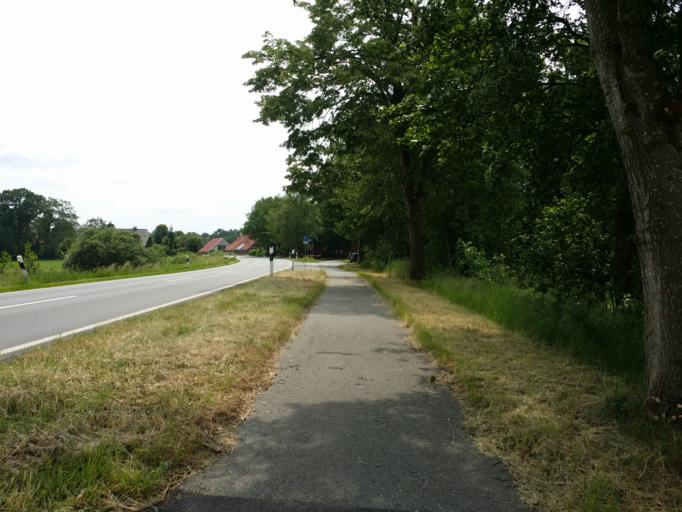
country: DE
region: Lower Saxony
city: Friedeburg
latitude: 53.4260
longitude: 7.8623
